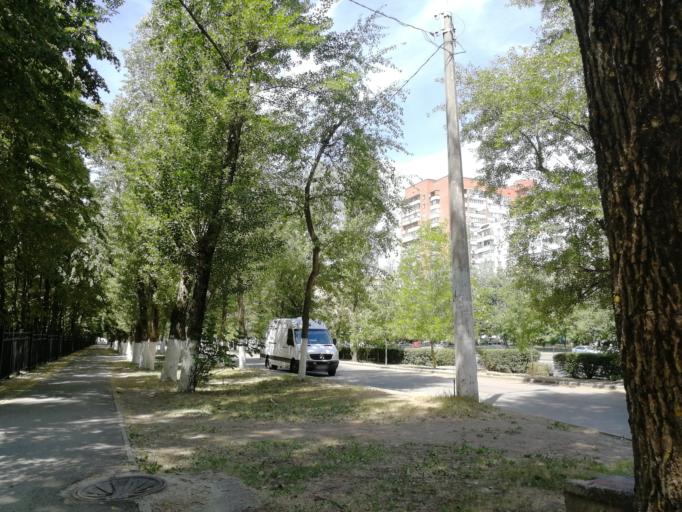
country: RU
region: Rostov
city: Rostov-na-Donu
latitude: 47.2248
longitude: 39.6220
